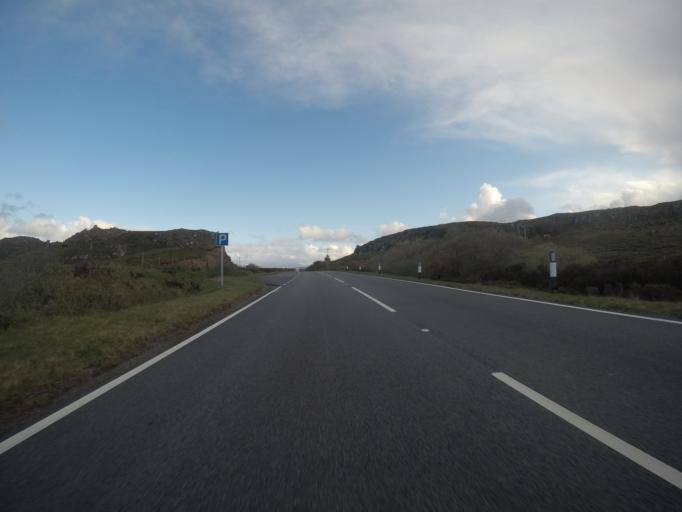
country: GB
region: Scotland
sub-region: Highland
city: Portree
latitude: 57.5164
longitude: -6.3420
